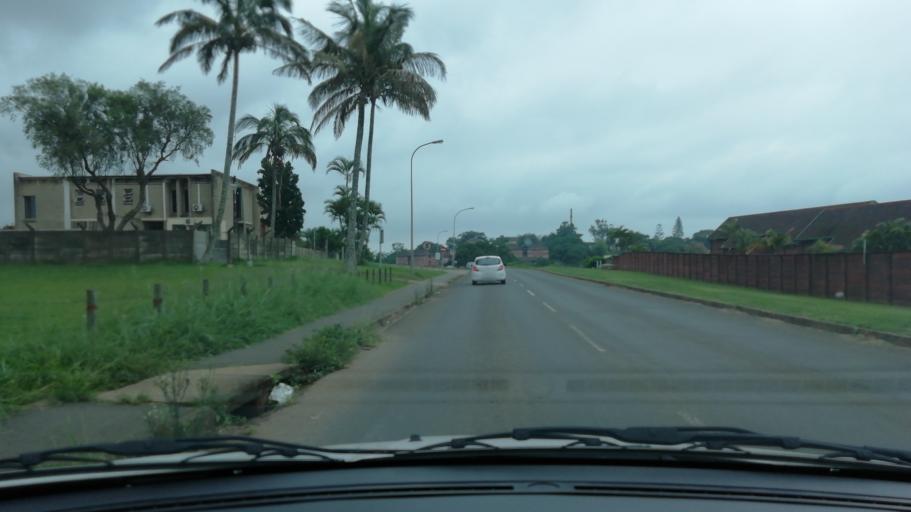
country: ZA
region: KwaZulu-Natal
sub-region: uThungulu District Municipality
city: Empangeni
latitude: -28.7503
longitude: 31.8854
